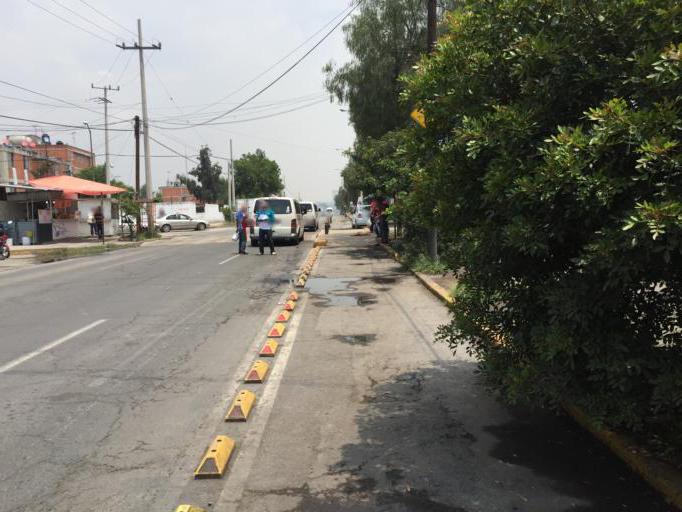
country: MX
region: Mexico
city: Cuautitlan Izcalli
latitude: 19.6391
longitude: -99.2070
